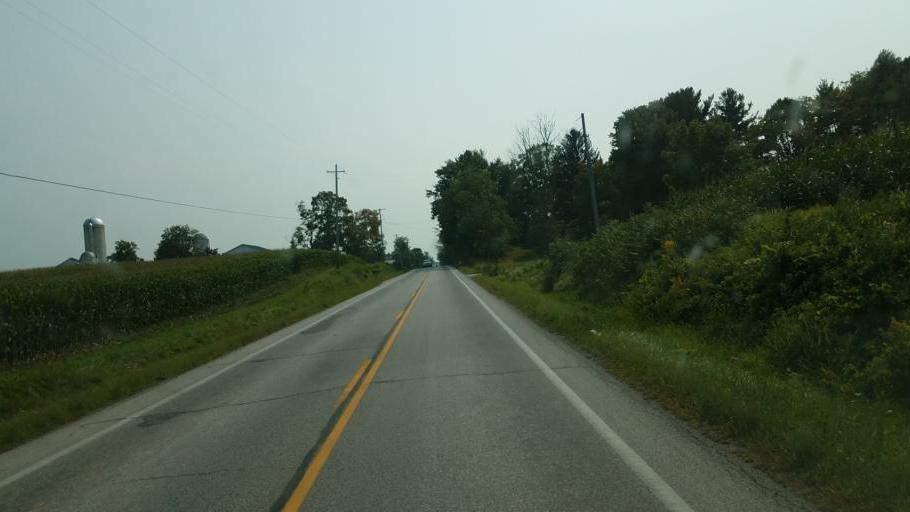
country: US
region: Ohio
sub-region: Ashtabula County
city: Orwell
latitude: 41.4863
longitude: -80.9474
